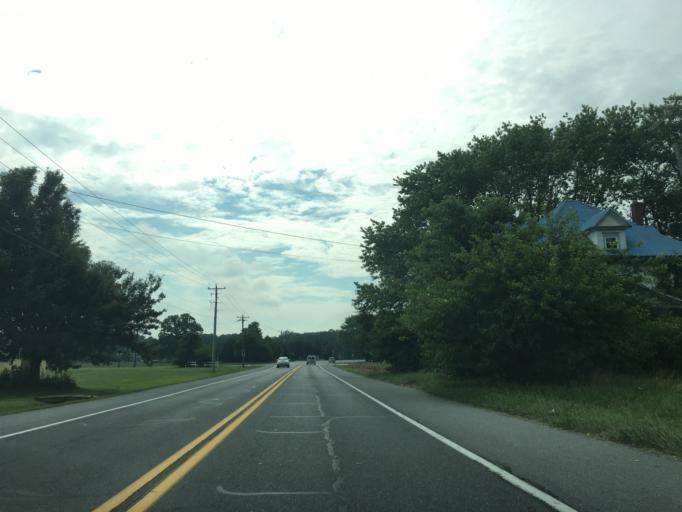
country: US
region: Delaware
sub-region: Sussex County
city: Long Neck
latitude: 38.5537
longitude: -75.1902
